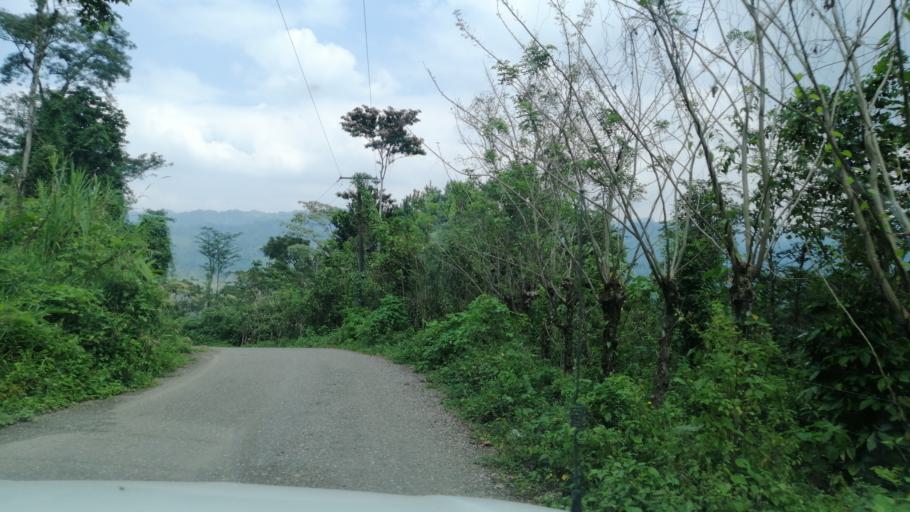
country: MX
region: Chiapas
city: Ostuacan
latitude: 17.3929
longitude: -93.3302
